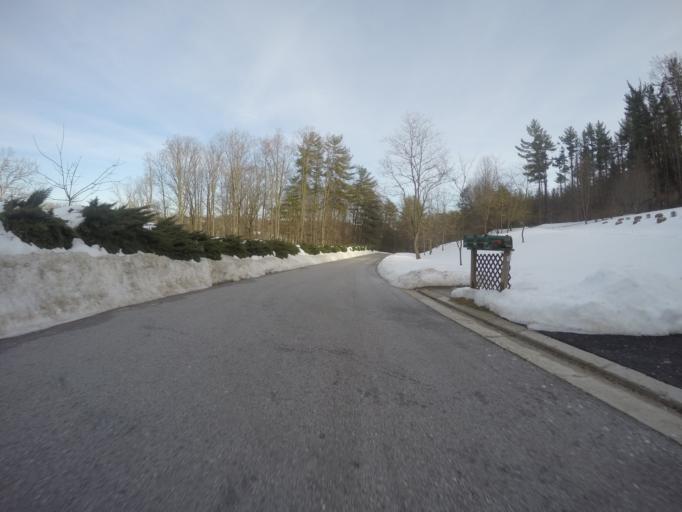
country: US
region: Maryland
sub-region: Baltimore County
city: Hunt Valley
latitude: 39.5617
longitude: -76.6105
